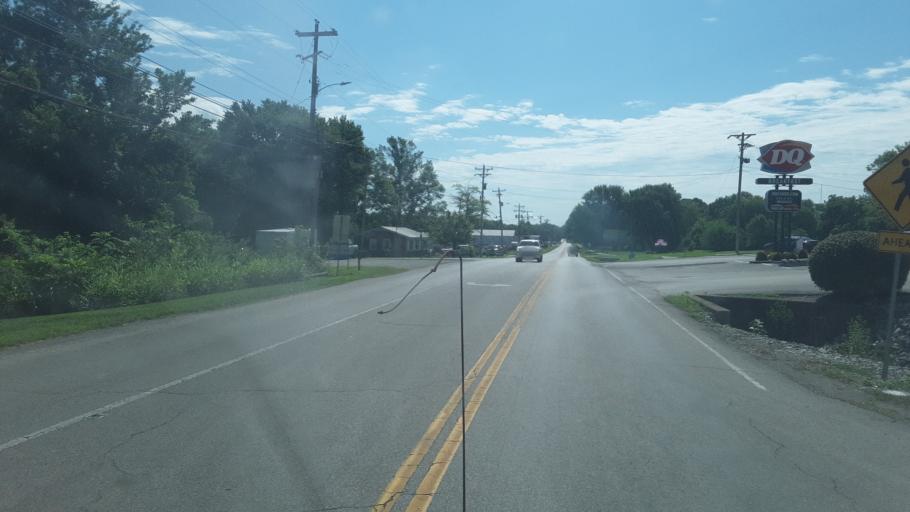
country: US
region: Kentucky
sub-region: Todd County
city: Elkton
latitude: 36.8127
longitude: -87.1680
